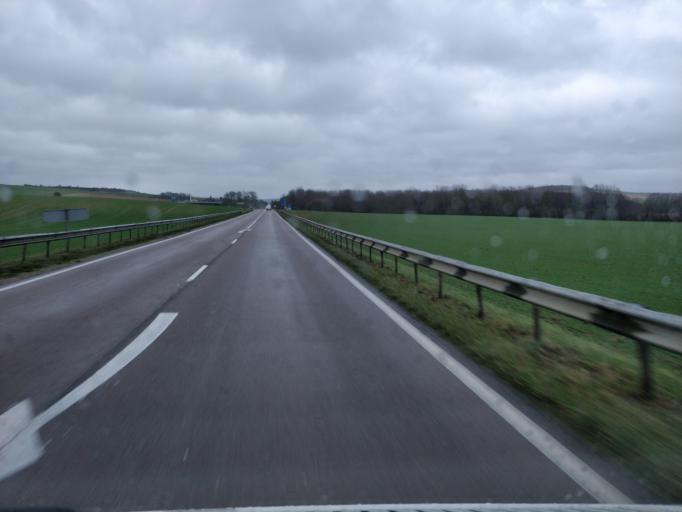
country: FR
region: Champagne-Ardenne
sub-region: Departement de l'Aube
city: Aix-en-Othe
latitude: 48.2349
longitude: 3.5969
